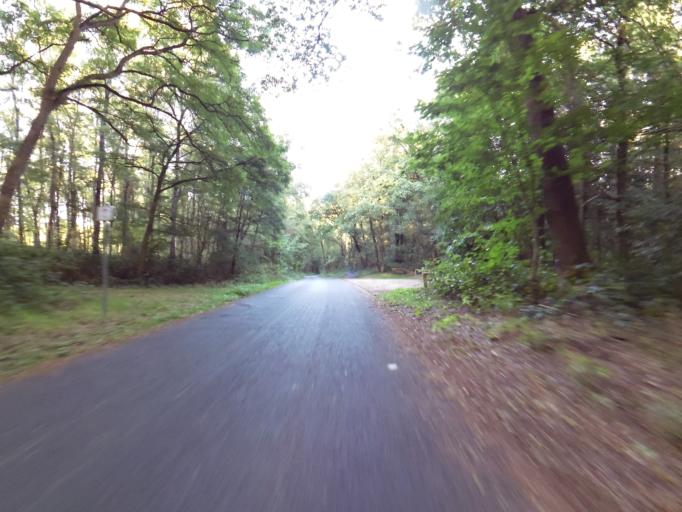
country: DE
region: North Rhine-Westphalia
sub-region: Regierungsbezirk Dusseldorf
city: Emmerich
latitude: 51.8661
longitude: 6.1793
